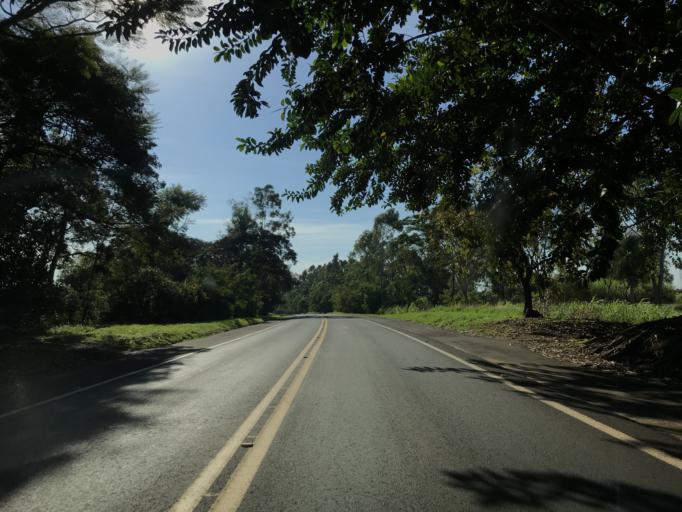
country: BR
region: Parana
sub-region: Ipora
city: Ipora
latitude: -23.9498
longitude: -53.5975
